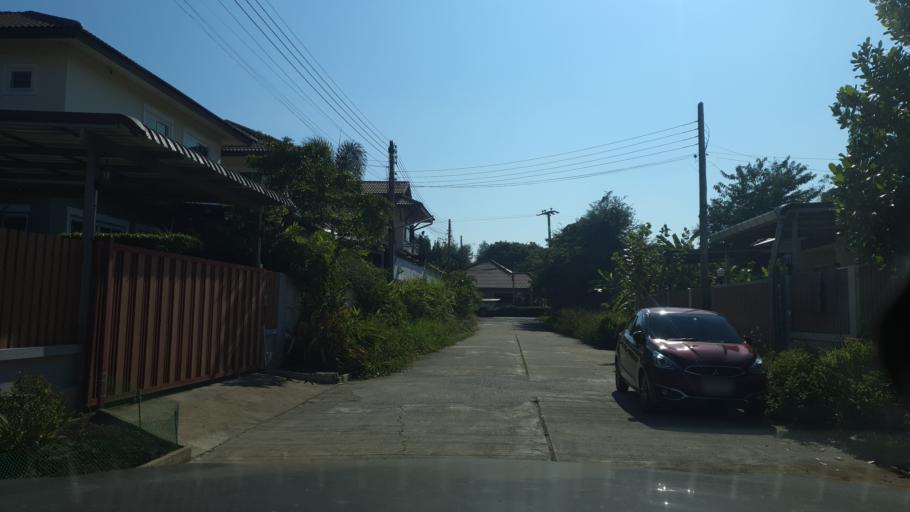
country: TH
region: Chiang Mai
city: Saraphi
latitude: 18.7252
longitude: 99.0611
